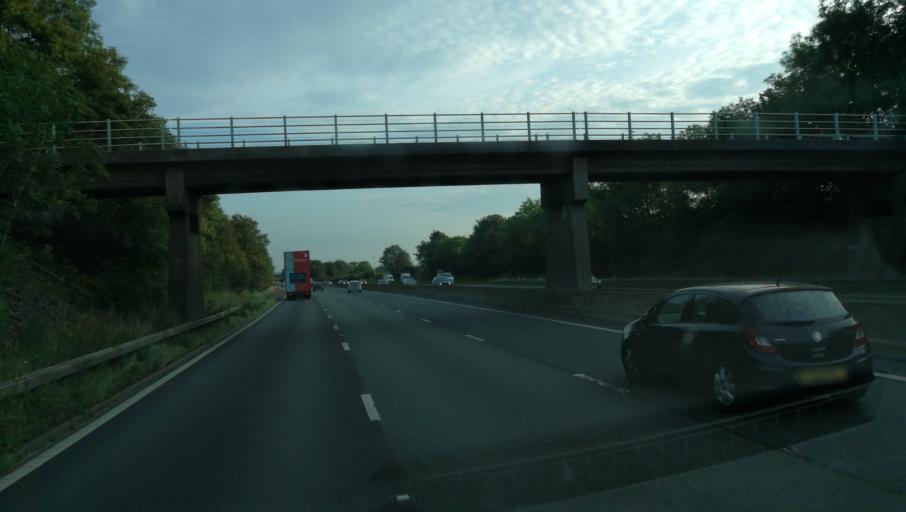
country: GB
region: England
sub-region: Lancashire
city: Lancaster
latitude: 54.0306
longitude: -2.7793
